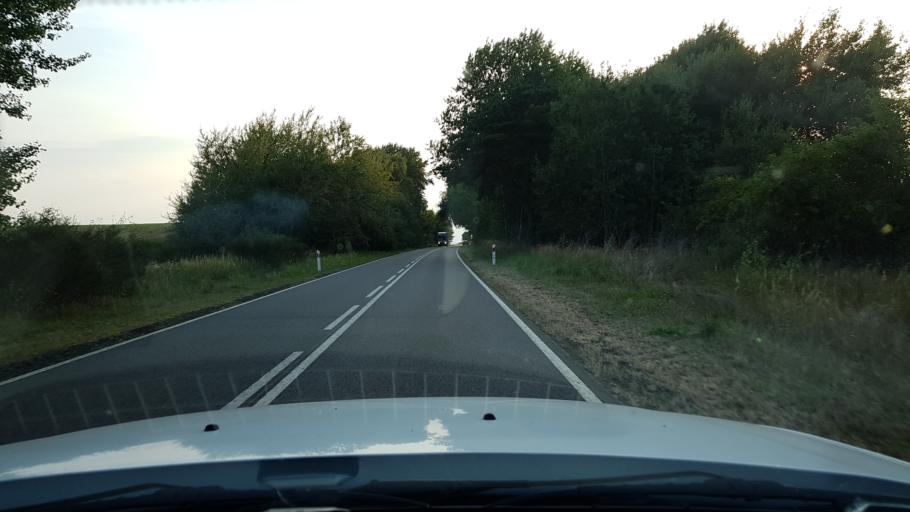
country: PL
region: West Pomeranian Voivodeship
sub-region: Powiat stargardzki
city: Marianowo
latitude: 53.4284
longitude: 15.2708
